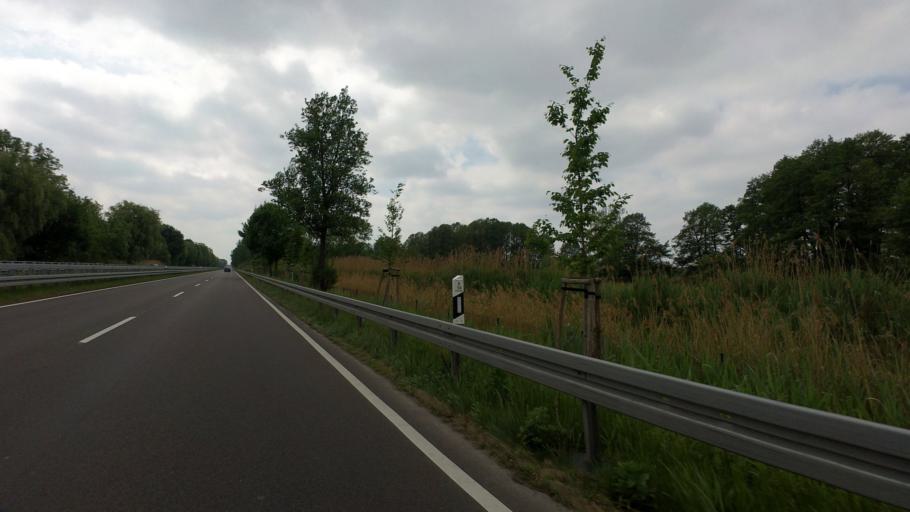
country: DE
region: Brandenburg
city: Peitz
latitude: 51.8399
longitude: 14.3878
